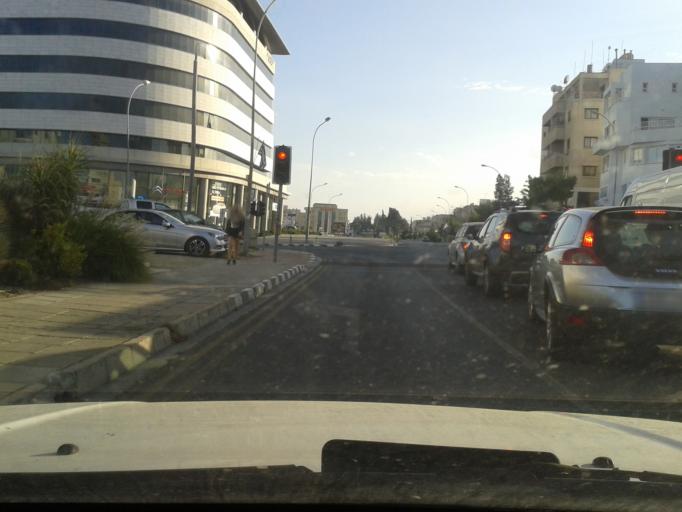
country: CY
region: Lefkosia
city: Nicosia
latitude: 35.1459
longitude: 33.3601
